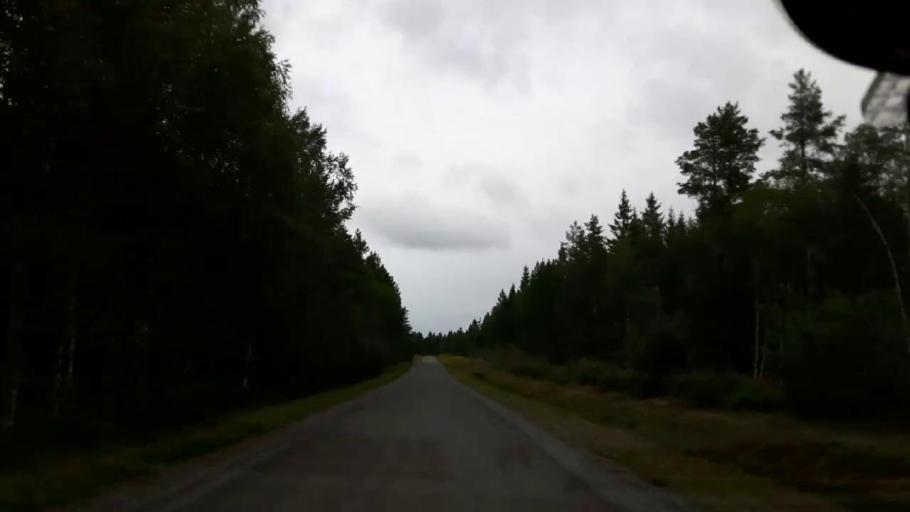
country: SE
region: Jaemtland
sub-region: OEstersunds Kommun
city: Ostersund
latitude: 63.0747
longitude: 14.5539
